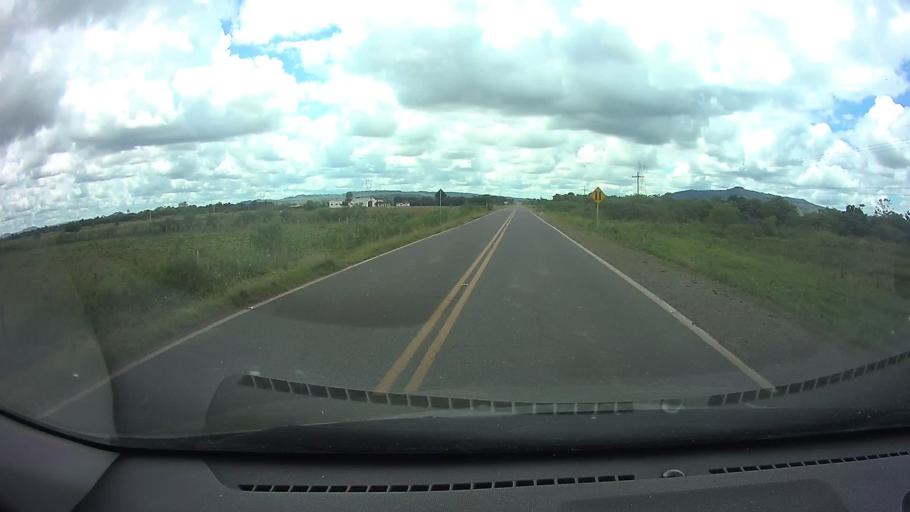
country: PY
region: Paraguari
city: Ybycui
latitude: -25.9131
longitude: -57.0276
